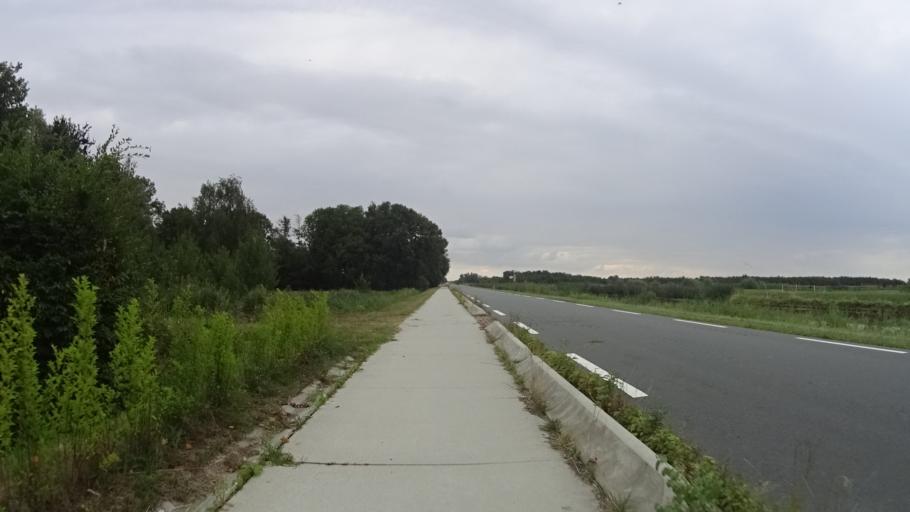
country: NL
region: Groningen
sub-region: Gemeente Groningen
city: Oosterpark
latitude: 53.2356
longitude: 6.6698
